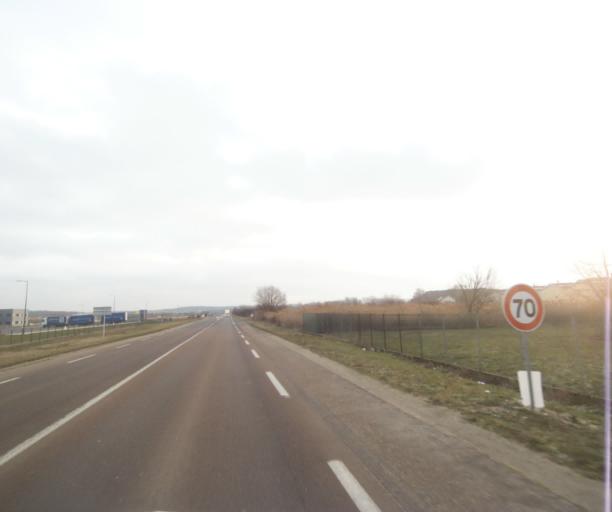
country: FR
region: Champagne-Ardenne
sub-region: Departement de la Haute-Marne
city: Saint-Dizier
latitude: 48.6490
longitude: 4.9434
